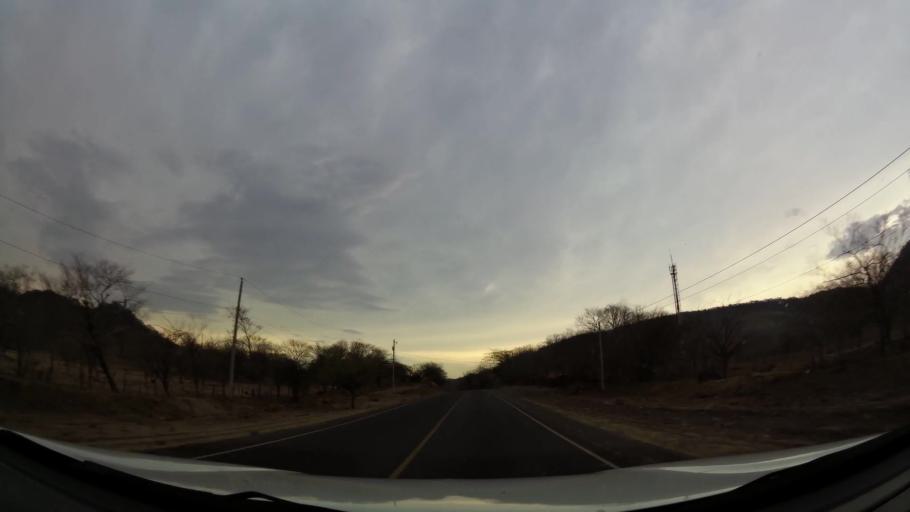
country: NI
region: Leon
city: La Jicaral
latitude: 12.6885
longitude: -86.4128
